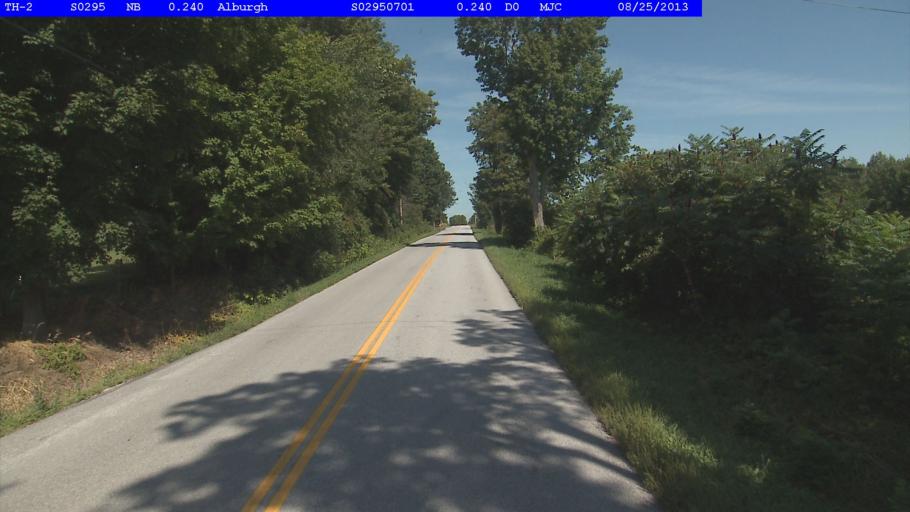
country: US
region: Vermont
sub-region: Franklin County
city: Swanton
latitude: 44.9781
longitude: -73.2308
